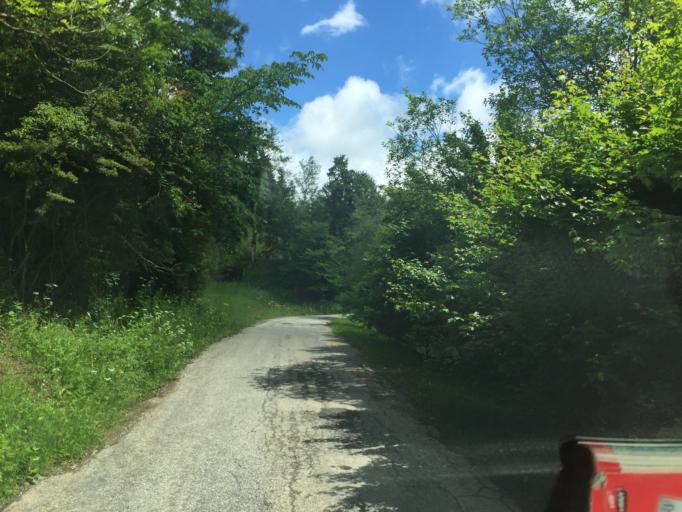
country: FR
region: Rhone-Alpes
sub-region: Departement de la Savoie
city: Cruet
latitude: 45.6159
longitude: 6.1116
